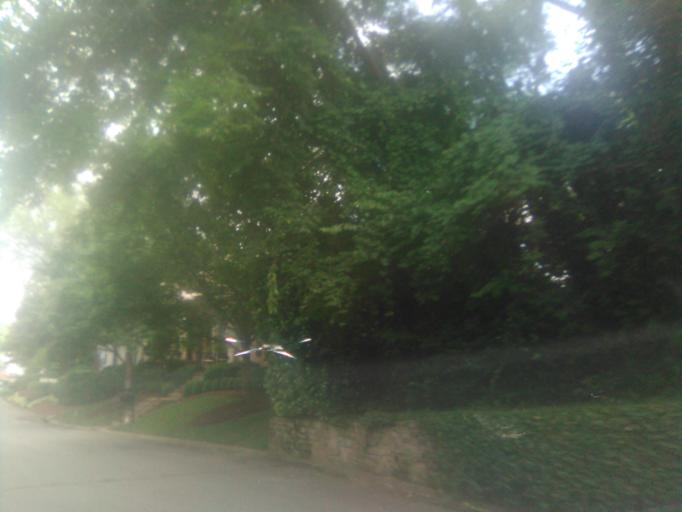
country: US
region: Tennessee
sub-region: Davidson County
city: Belle Meade
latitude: 36.1079
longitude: -86.8298
